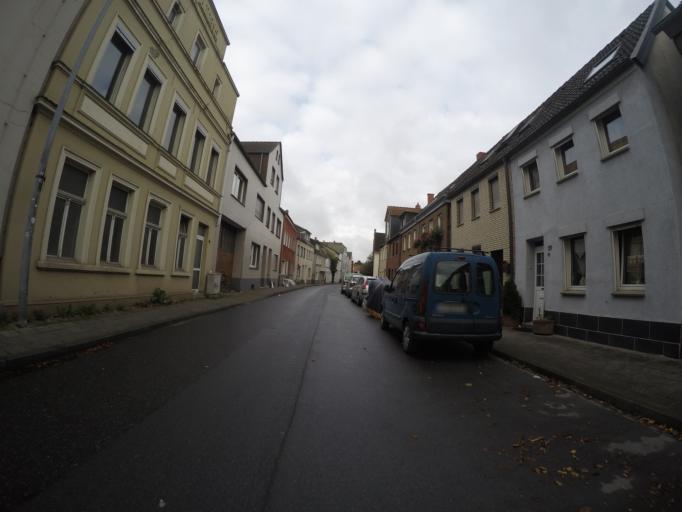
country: DE
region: North Rhine-Westphalia
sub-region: Regierungsbezirk Arnsberg
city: Lippstadt
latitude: 51.6716
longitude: 8.3417
